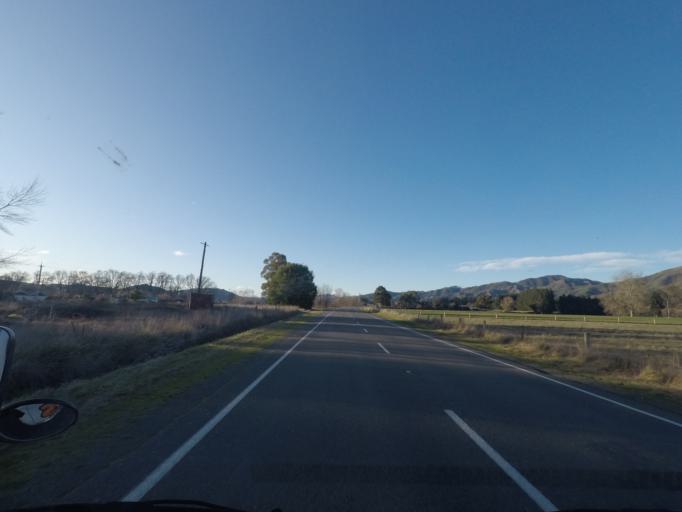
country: NZ
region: Canterbury
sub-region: Kaikoura District
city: Kaikoura
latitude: -42.7117
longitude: 173.2918
